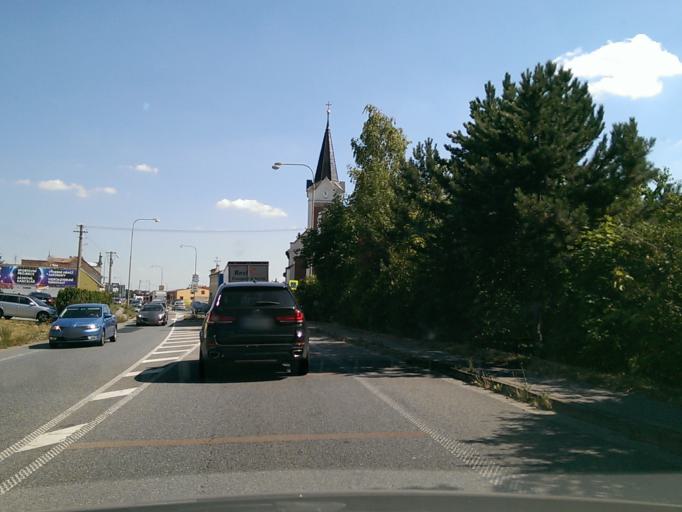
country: CZ
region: South Moravian
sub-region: Okres Breclav
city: Mikulov
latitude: 48.8023
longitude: 16.6278
